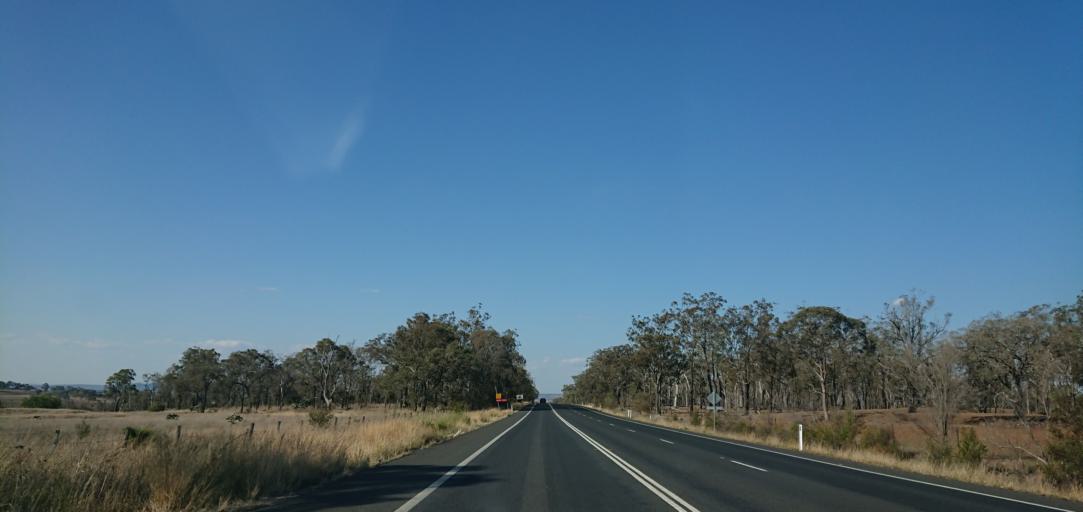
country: AU
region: Queensland
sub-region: Toowoomba
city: Westbrook
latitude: -27.6246
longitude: 151.7611
